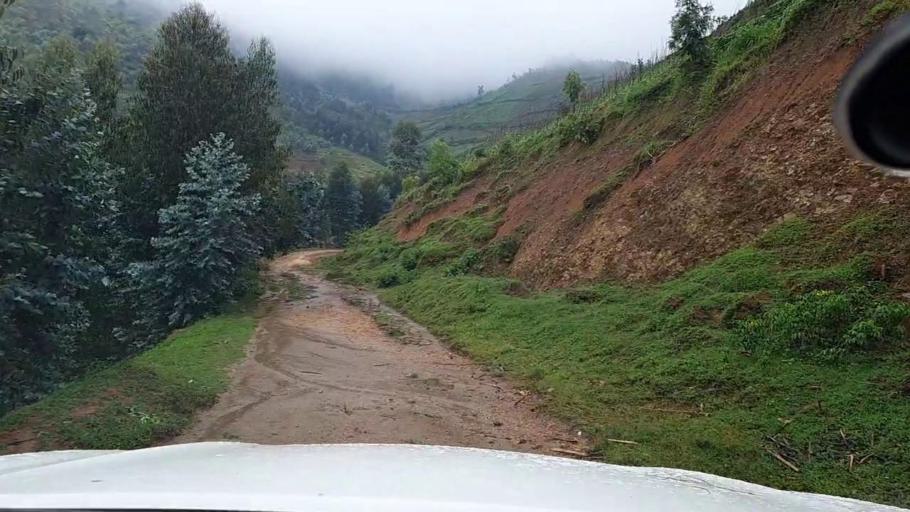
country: RW
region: Western Province
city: Kibuye
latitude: -2.1463
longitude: 29.4593
